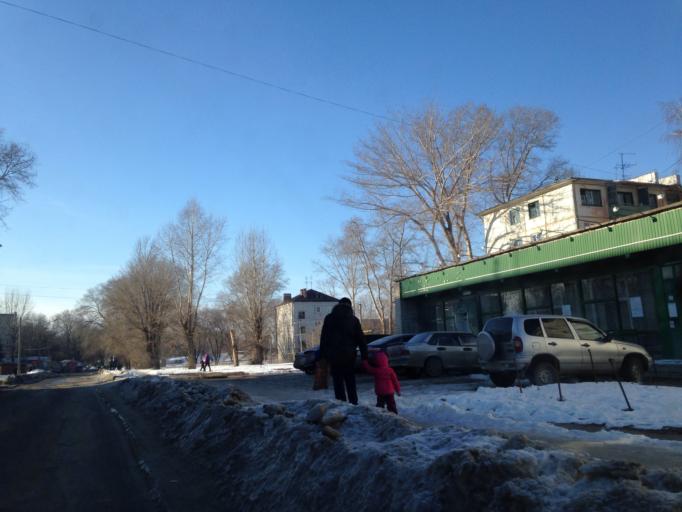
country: RU
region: Ulyanovsk
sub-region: Ulyanovskiy Rayon
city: Ulyanovsk
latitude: 54.2923
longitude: 48.3184
